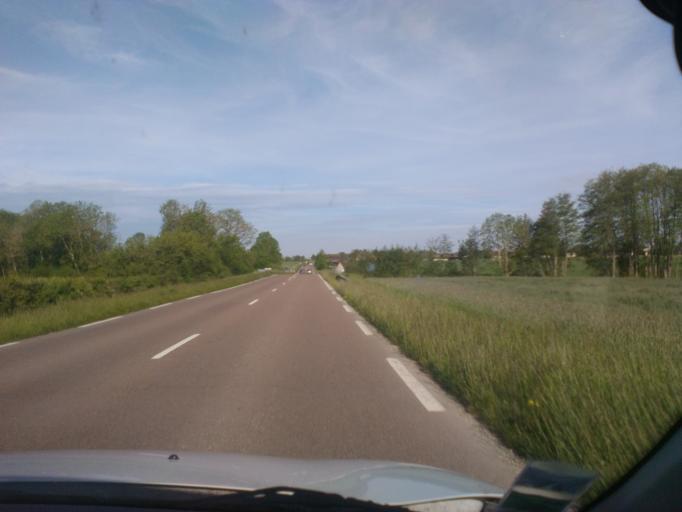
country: FR
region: Champagne-Ardenne
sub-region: Departement de l'Aube
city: Vendeuvre-sur-Barse
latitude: 48.2339
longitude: 4.4020
